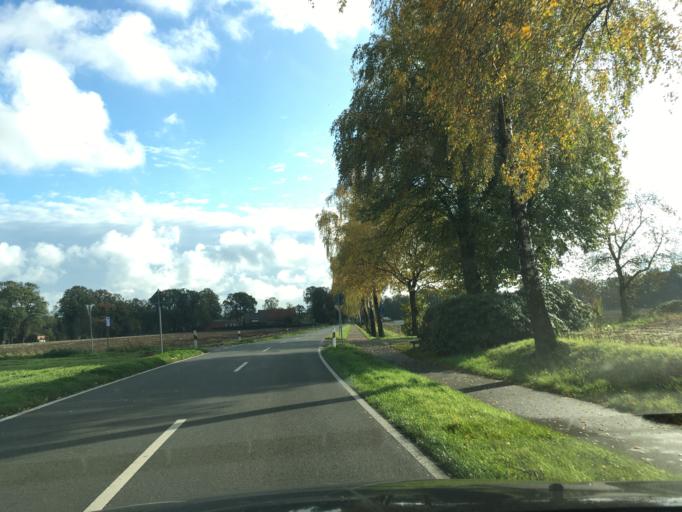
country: DE
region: North Rhine-Westphalia
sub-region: Regierungsbezirk Munster
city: Vreden
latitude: 52.0963
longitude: 6.8642
